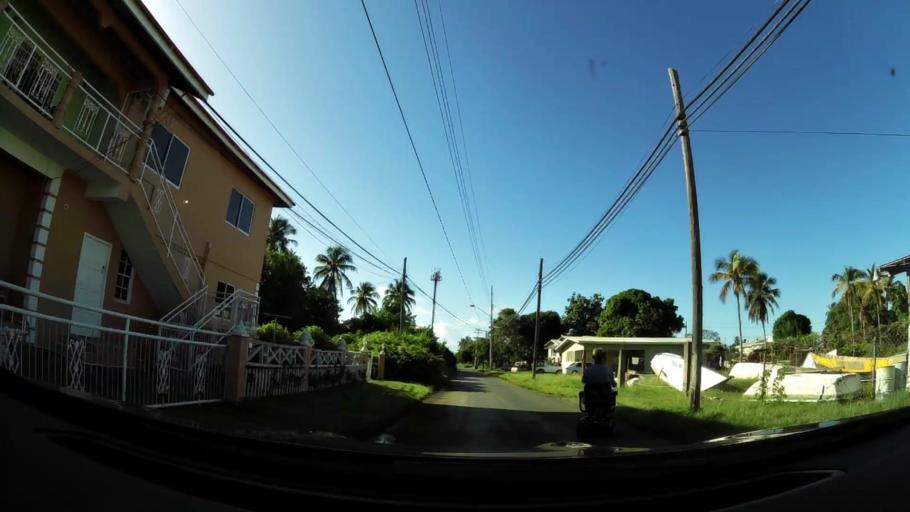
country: TT
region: Tobago
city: Scarborough
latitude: 11.1541
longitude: -60.8262
